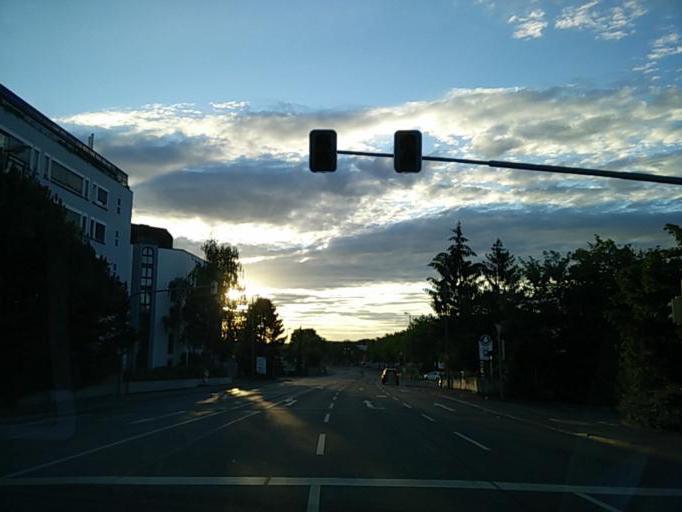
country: DE
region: Baden-Wuerttemberg
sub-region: Regierungsbezirk Stuttgart
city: Boeblingen
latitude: 48.6849
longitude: 8.9984
